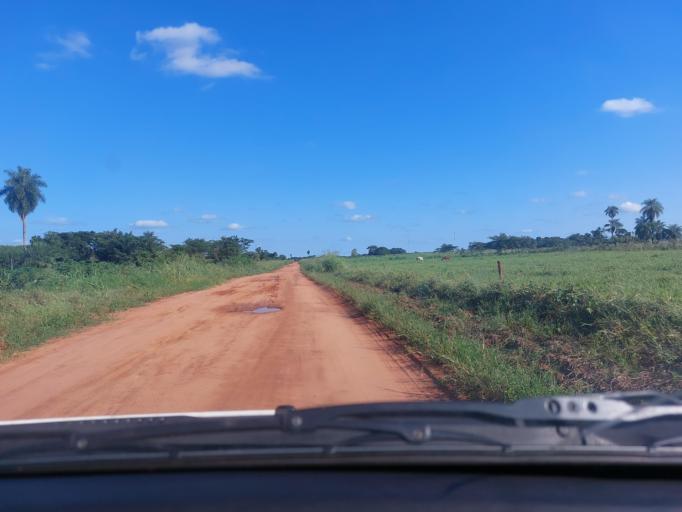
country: PY
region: San Pedro
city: Guayaybi
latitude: -24.5155
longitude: -56.5463
